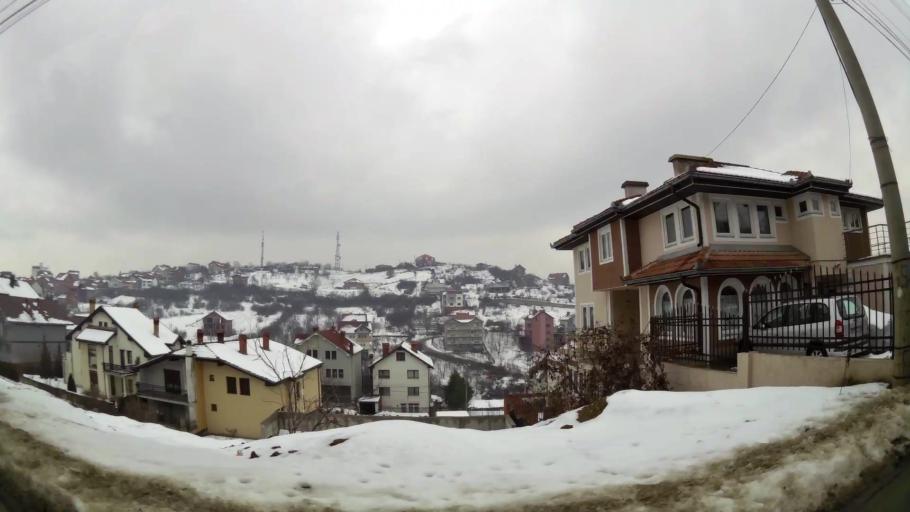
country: XK
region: Pristina
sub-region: Komuna e Prishtines
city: Pristina
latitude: 42.6755
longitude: 21.1843
